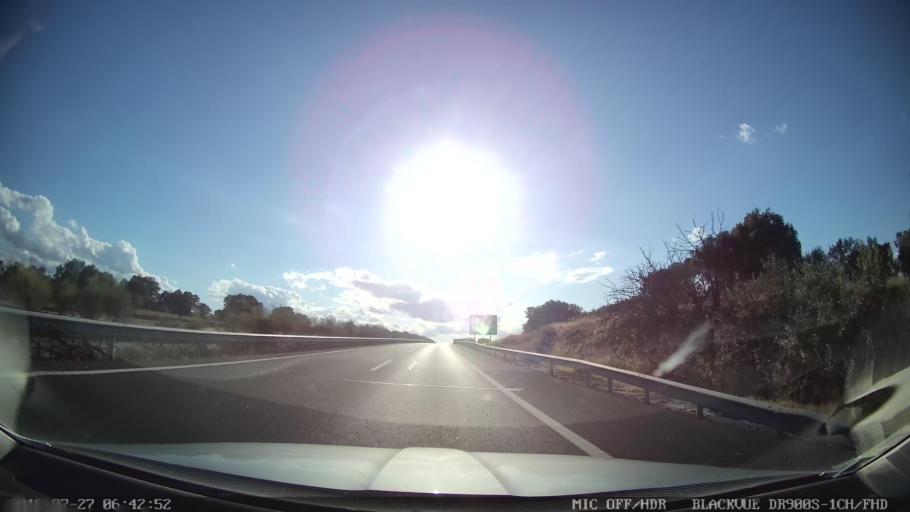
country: ES
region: Extremadura
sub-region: Provincia de Caceres
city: Peraleda de la Mata
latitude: 39.8898
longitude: -5.4915
